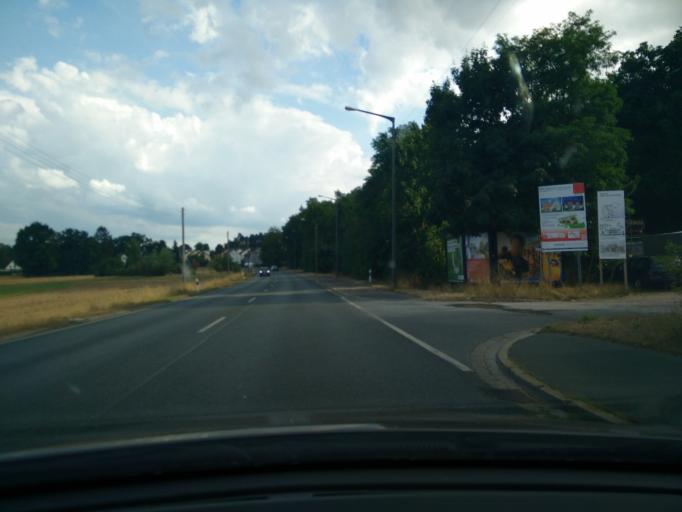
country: DE
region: Bavaria
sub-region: Regierungsbezirk Mittelfranken
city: Schwabach
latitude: 49.3720
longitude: 11.0269
